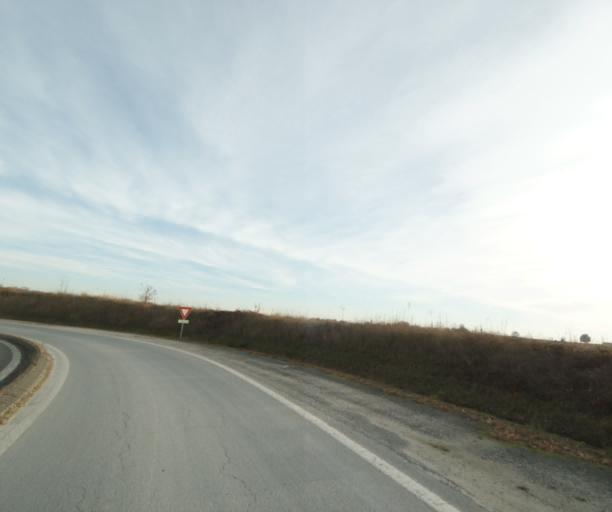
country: FR
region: Poitou-Charentes
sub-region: Departement de la Charente-Maritime
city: Saint-Porchaire
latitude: 45.8108
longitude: -0.7681
